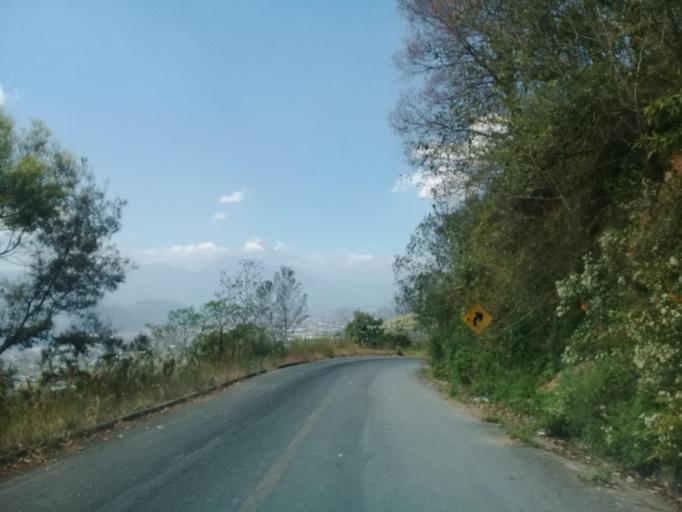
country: MX
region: Veracruz
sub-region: Tlilapan
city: Tonalixco
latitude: 18.8091
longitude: -97.0608
